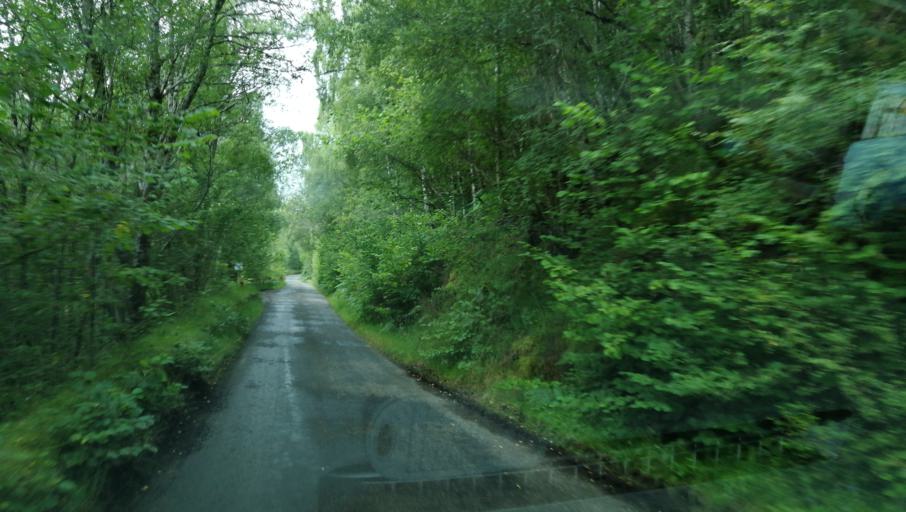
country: GB
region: Scotland
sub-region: Highland
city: Beauly
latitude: 57.3160
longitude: -4.8342
